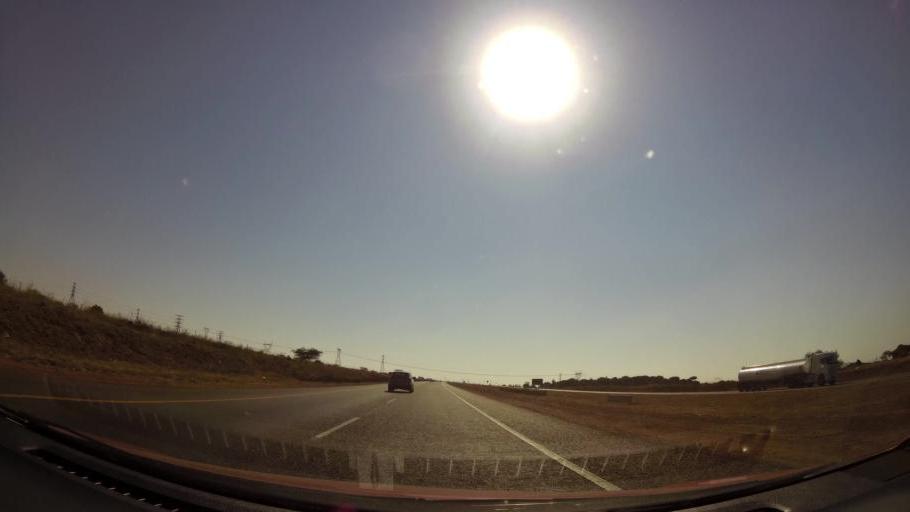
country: ZA
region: Gauteng
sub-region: City of Tshwane Metropolitan Municipality
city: Mabopane
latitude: -25.5671
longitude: 28.1075
